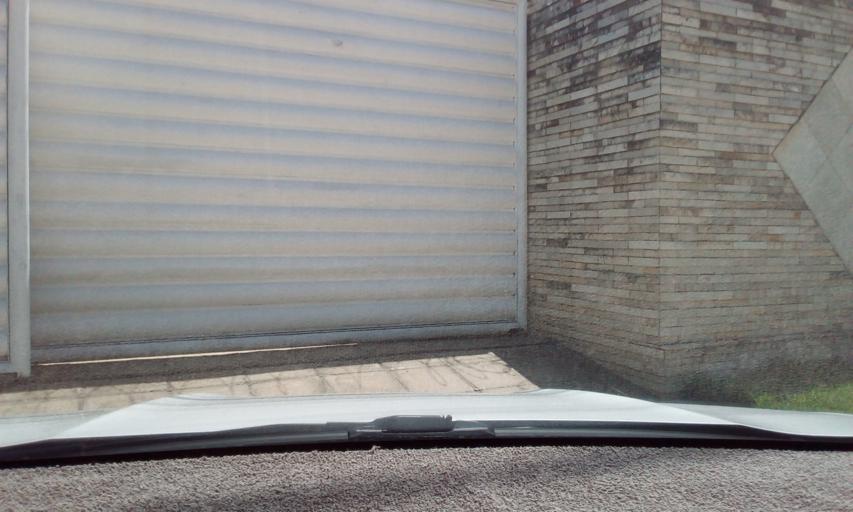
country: BR
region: Paraiba
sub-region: Joao Pessoa
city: Joao Pessoa
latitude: -7.0850
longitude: -34.8368
